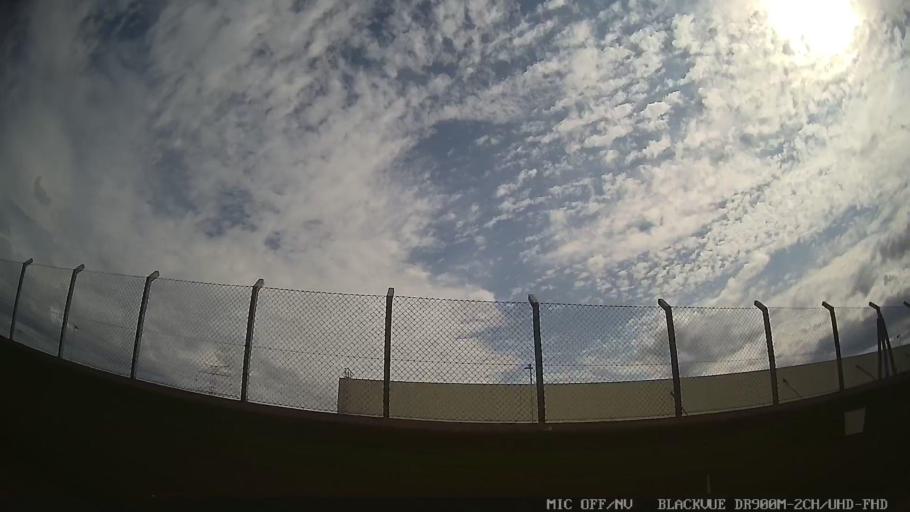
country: BR
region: Sao Paulo
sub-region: Salto
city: Salto
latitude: -23.1615
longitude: -47.2658
